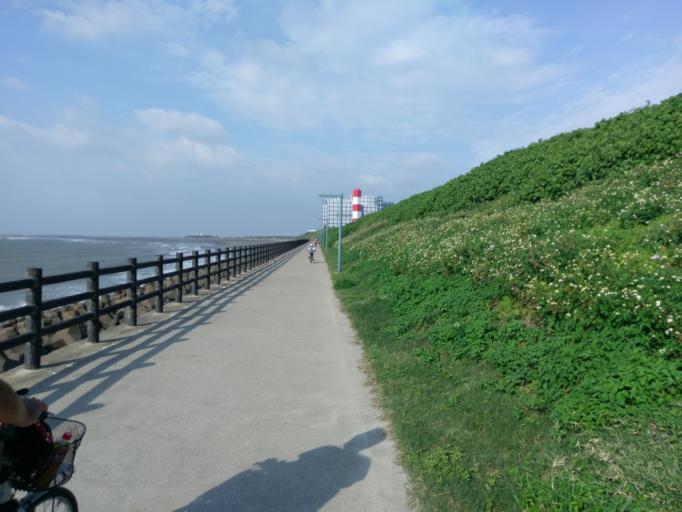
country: TW
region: Taiwan
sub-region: Hsinchu
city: Hsinchu
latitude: 24.8292
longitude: 120.9123
